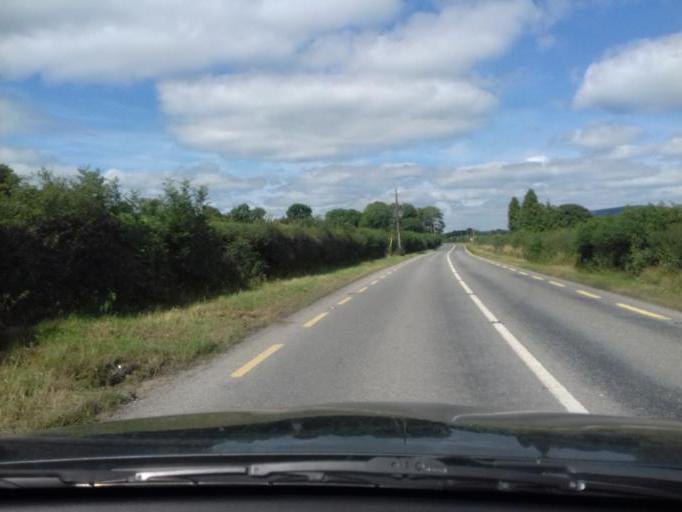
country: IE
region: Leinster
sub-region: Wicklow
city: Baltinglass
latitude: 53.0048
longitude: -6.6436
